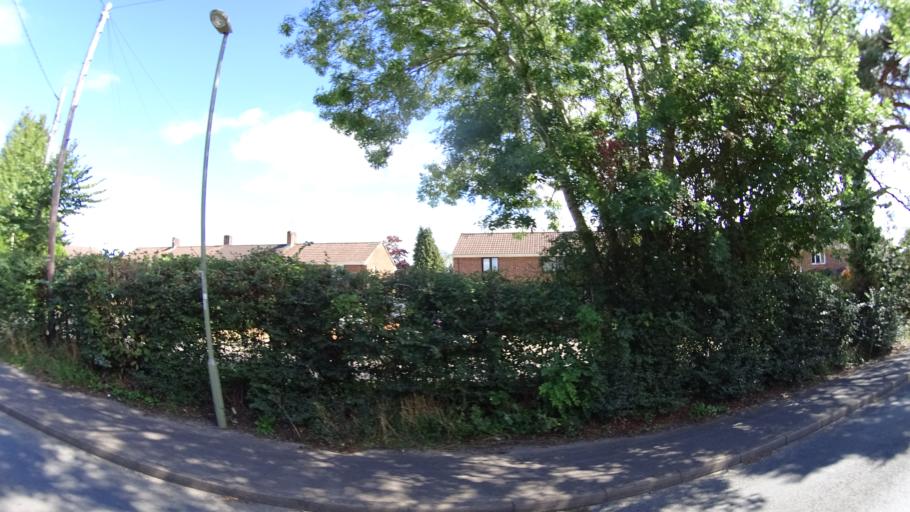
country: GB
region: England
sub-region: Hampshire
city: Romsey
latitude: 51.0017
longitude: -1.4728
